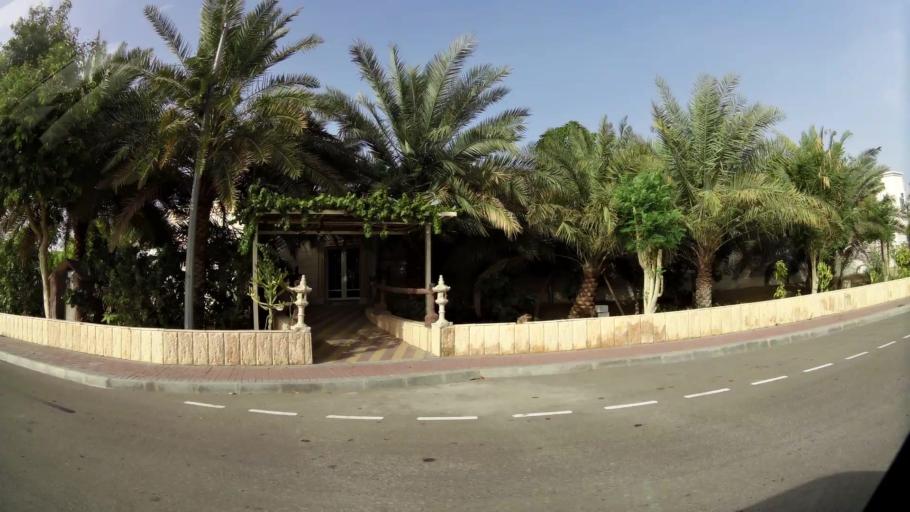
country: AE
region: Abu Dhabi
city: Al Ain
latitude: 24.2033
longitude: 55.6263
